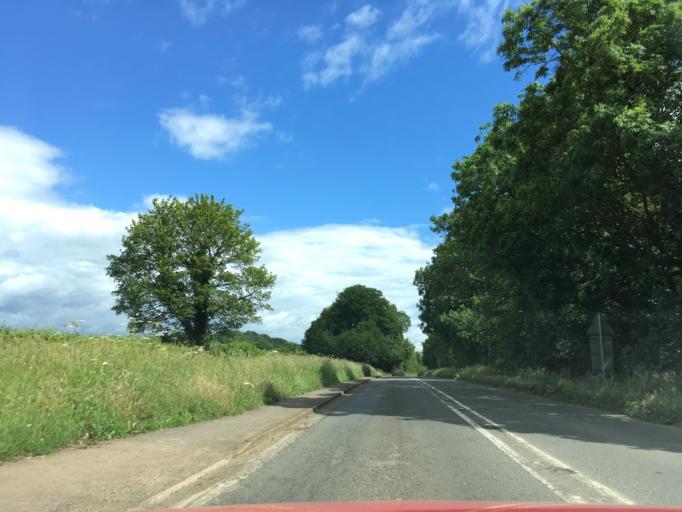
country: GB
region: England
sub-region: Oxfordshire
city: Bloxham
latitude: 52.0421
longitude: -1.3600
